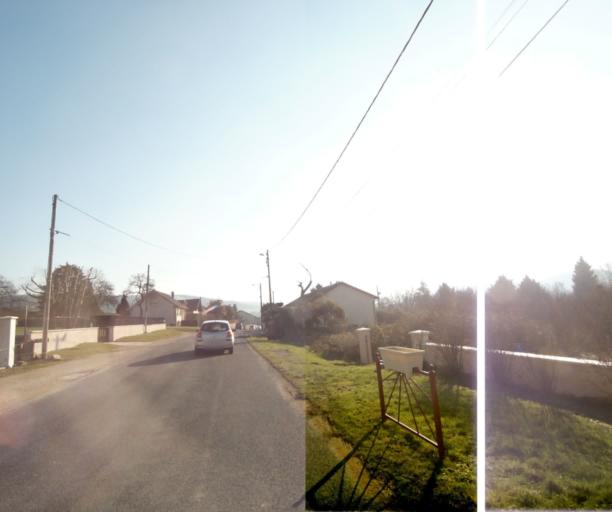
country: FR
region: Champagne-Ardenne
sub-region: Departement de la Haute-Marne
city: Chevillon
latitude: 48.4950
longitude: 5.1346
